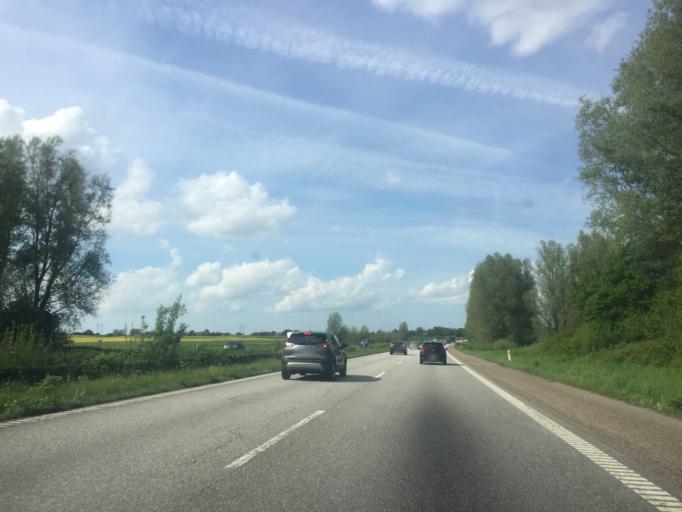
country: DK
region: Capital Region
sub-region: Fredensborg Kommune
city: Niva
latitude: 55.9449
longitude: 12.4786
